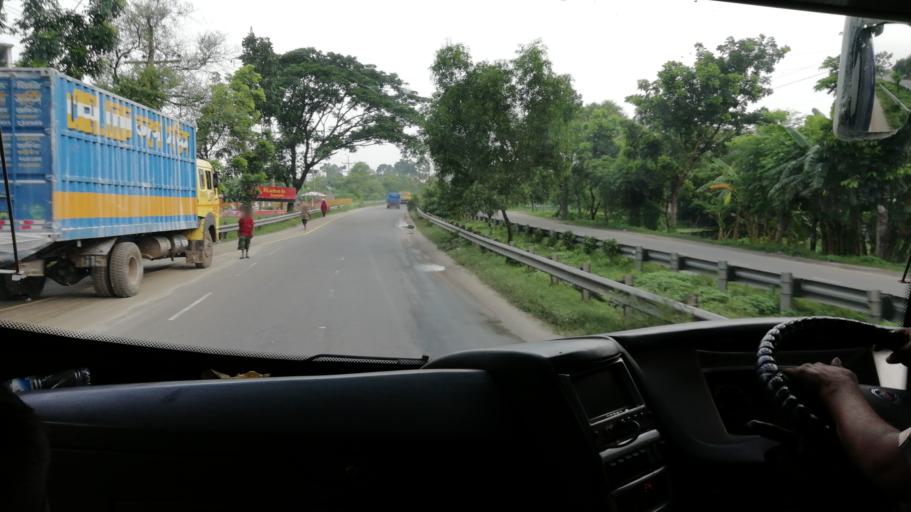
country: BD
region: Khulna
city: Khulna
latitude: 22.7867
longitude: 89.5356
